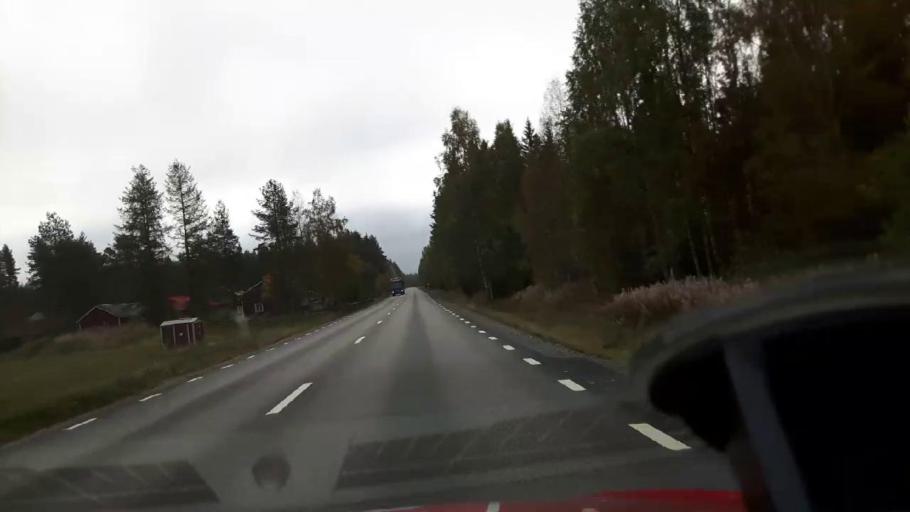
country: SE
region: Gaevleborg
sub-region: Ljusdals Kommun
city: Farila
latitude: 61.8585
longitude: 15.7439
